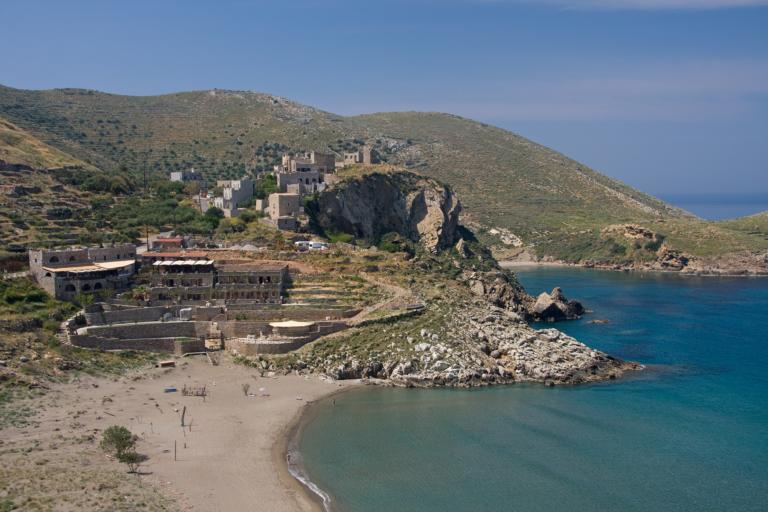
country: GR
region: Peloponnese
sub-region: Nomos Lakonias
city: Gytheio
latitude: 36.4279
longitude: 22.4768
